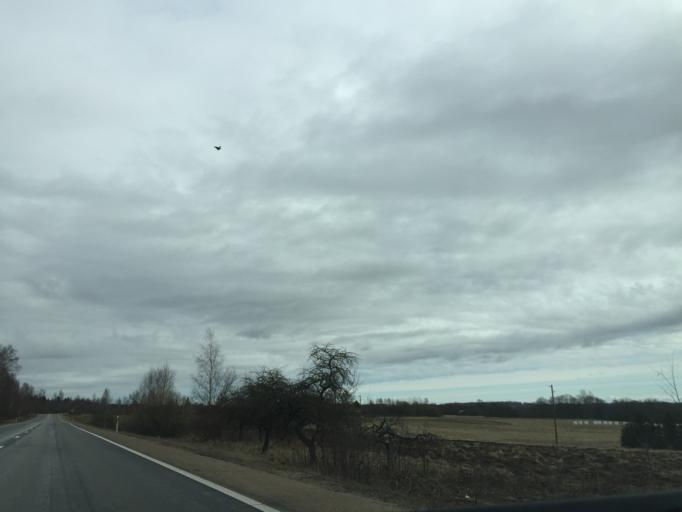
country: LV
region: Daugavpils
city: Daugavpils
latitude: 55.9230
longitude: 26.6792
